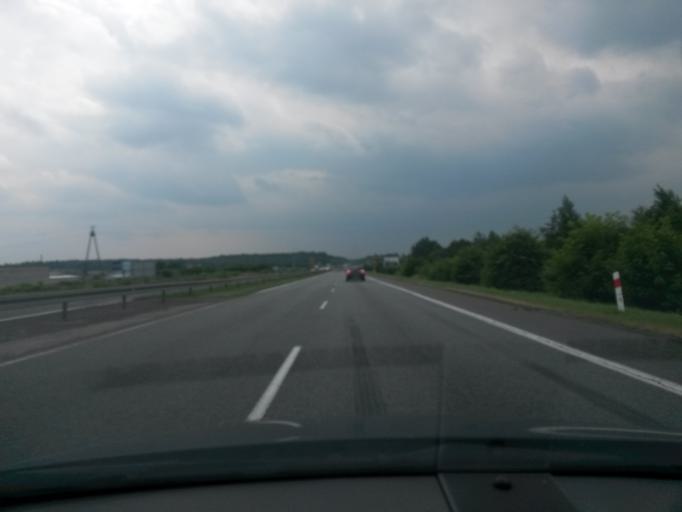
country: PL
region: Lodz Voivodeship
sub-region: Powiat radomszczanski
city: Radomsko
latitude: 51.0837
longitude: 19.3733
